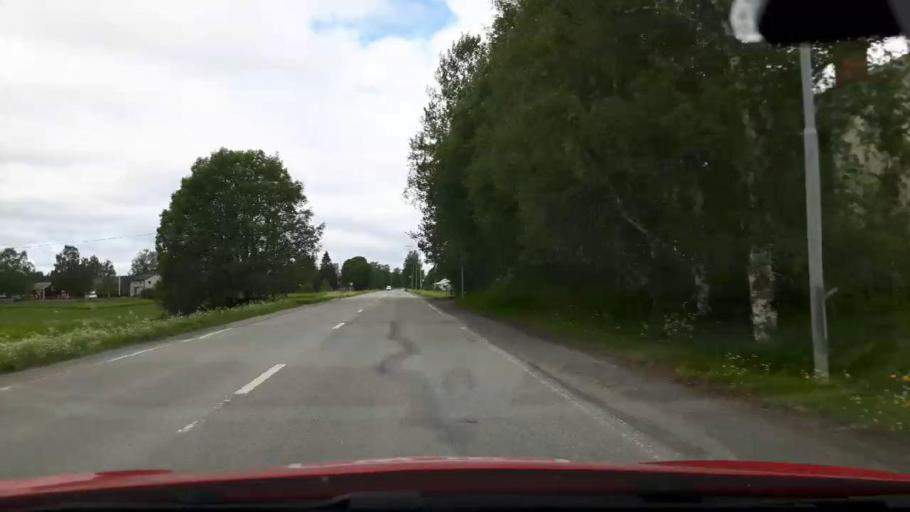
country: SE
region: Jaemtland
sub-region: Krokoms Kommun
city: Krokom
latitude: 63.3078
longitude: 14.4653
